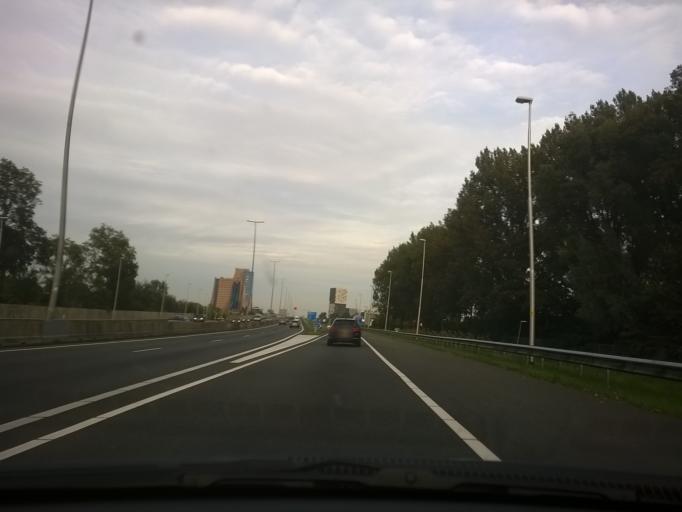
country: NL
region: Groningen
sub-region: Gemeente Groningen
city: Groningen
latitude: 53.1966
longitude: 6.5408
